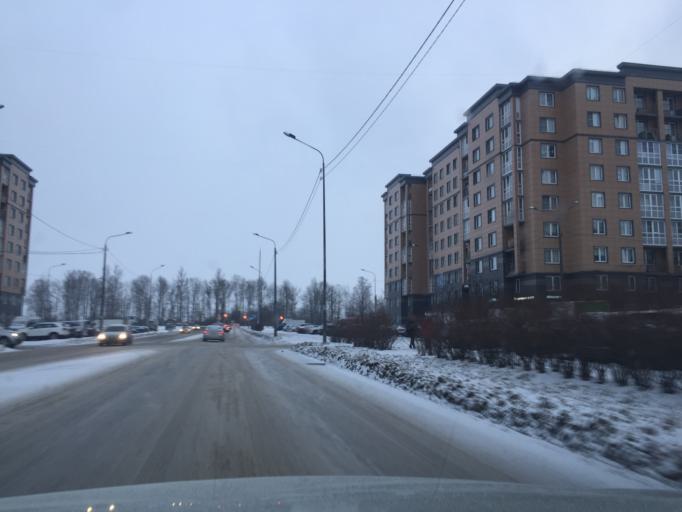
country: RU
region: St.-Petersburg
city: Tyarlevo
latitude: 59.7408
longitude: 30.4773
